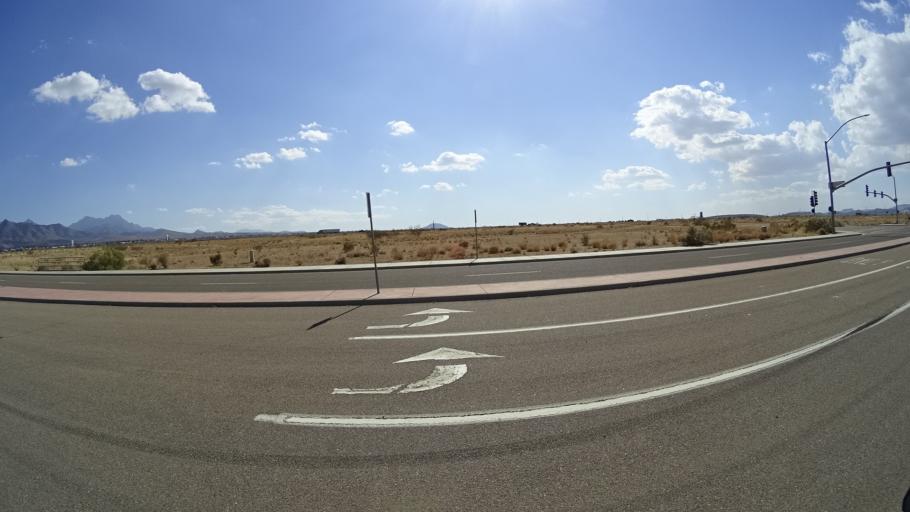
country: US
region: Arizona
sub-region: Mohave County
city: New Kingman-Butler
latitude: 35.2180
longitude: -113.9827
